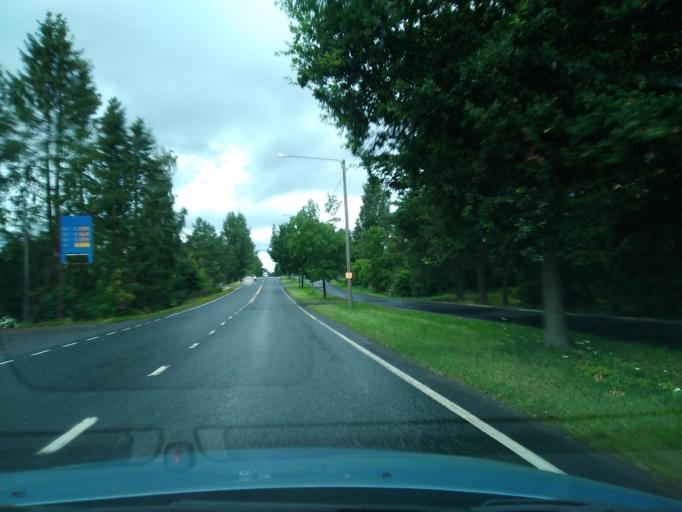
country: FI
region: Haeme
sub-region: Forssa
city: Tammela
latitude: 60.8070
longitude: 23.7736
